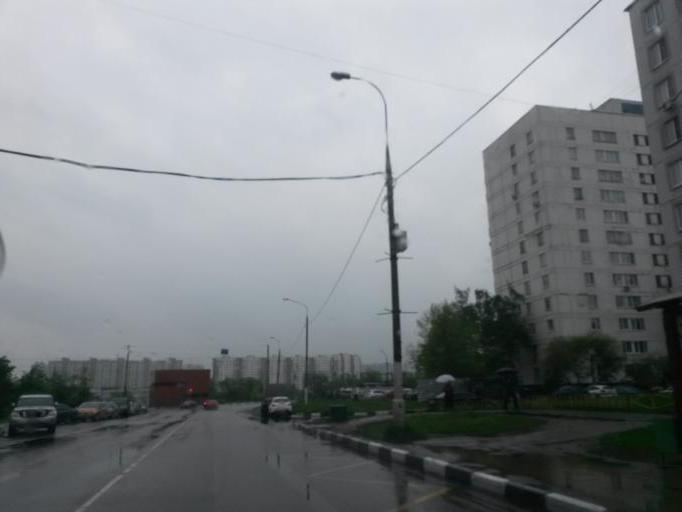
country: RU
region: Moscow
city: Zyablikovo
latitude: 55.6159
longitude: 37.7530
